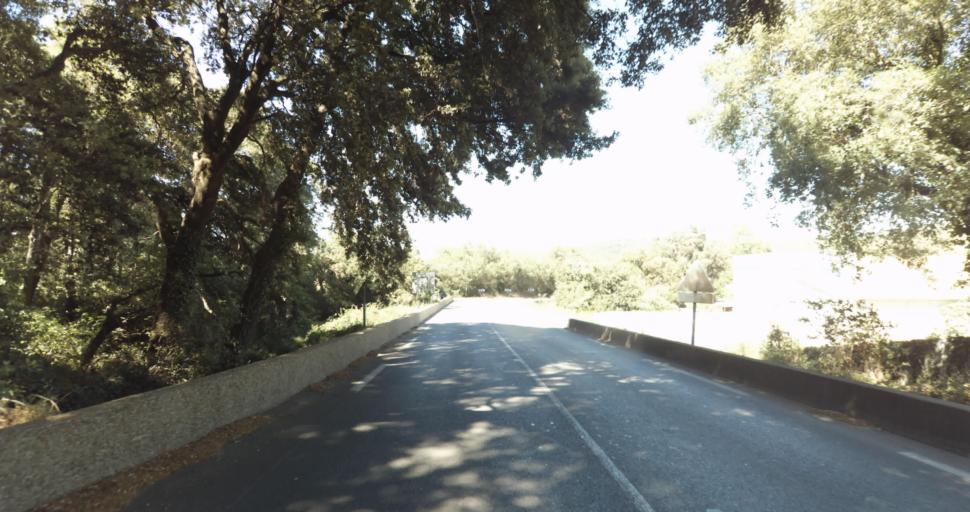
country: FR
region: Provence-Alpes-Cote d'Azur
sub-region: Departement du Var
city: La Croix-Valmer
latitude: 43.2152
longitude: 6.5683
